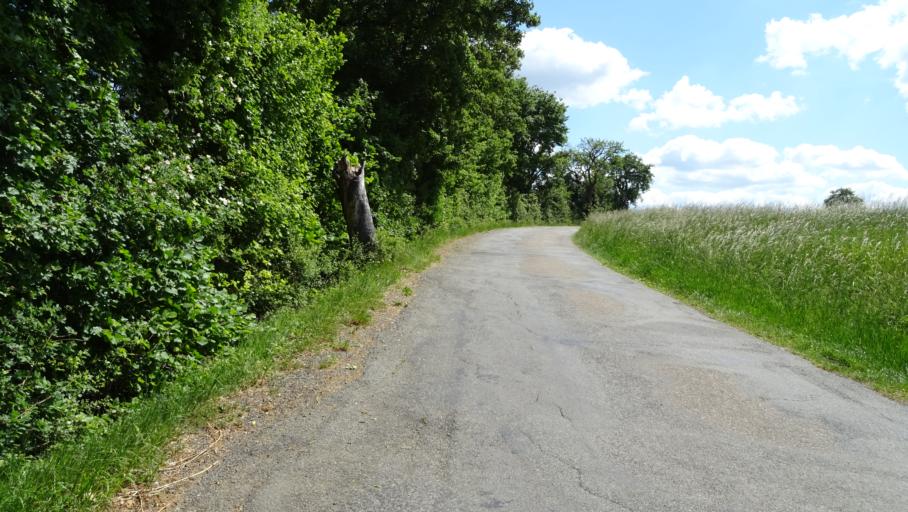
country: DE
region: Baden-Wuerttemberg
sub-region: Karlsruhe Region
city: Seckach
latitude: 49.4284
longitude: 9.3652
